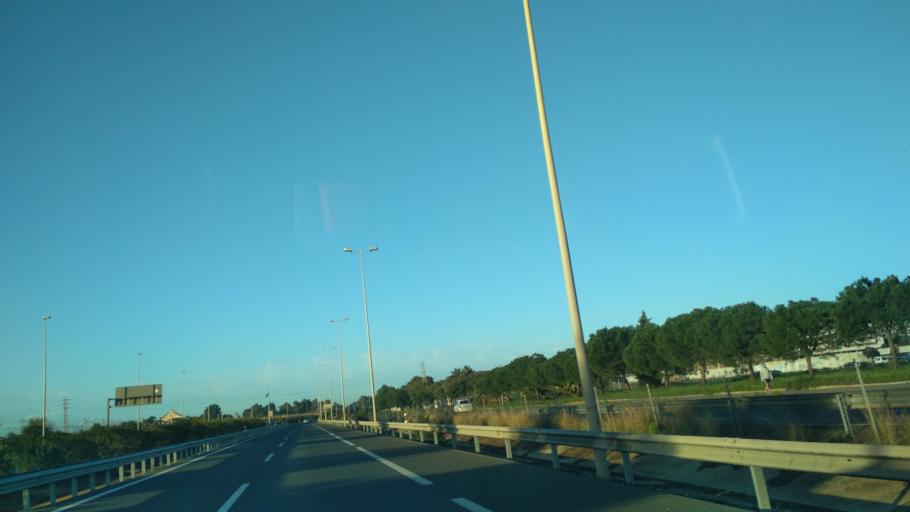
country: ES
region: Andalusia
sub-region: Provincia de Huelva
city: Huelva
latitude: 37.2561
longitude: -6.9250
